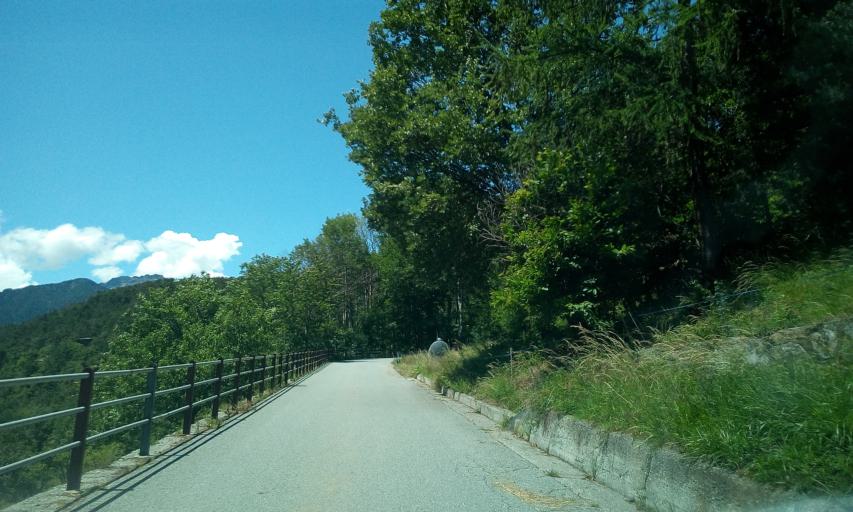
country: IT
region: Aosta Valley
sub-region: Valle d'Aosta
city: Challand-Saint-Victor
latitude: 45.6981
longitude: 7.7049
